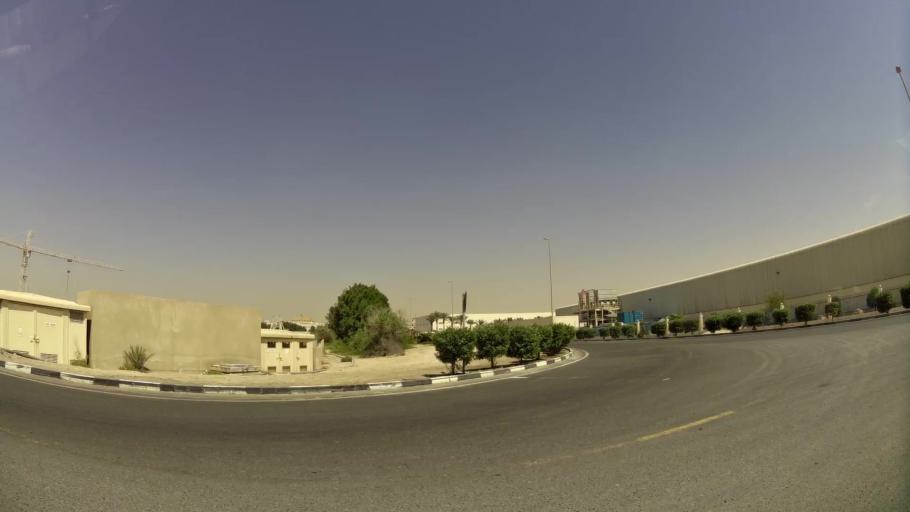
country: AE
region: Dubai
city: Dubai
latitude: 24.9743
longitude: 55.1597
